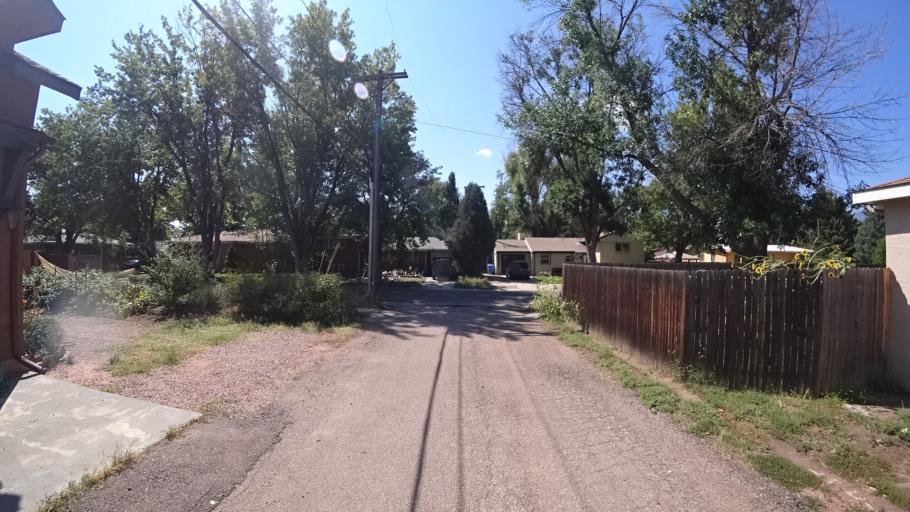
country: US
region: Colorado
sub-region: El Paso County
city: Colorado Springs
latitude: 38.8643
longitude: -104.8110
